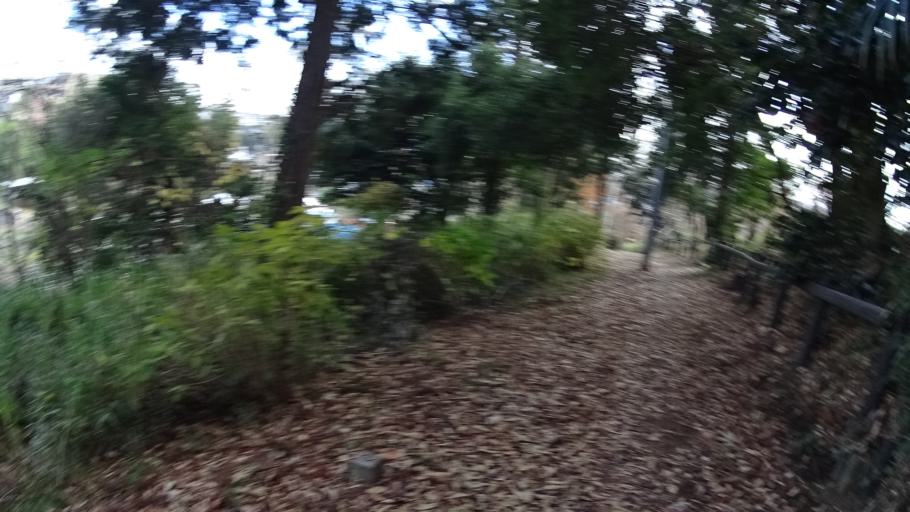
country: JP
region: Kanagawa
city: Yokohama
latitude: 35.4151
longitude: 139.5575
